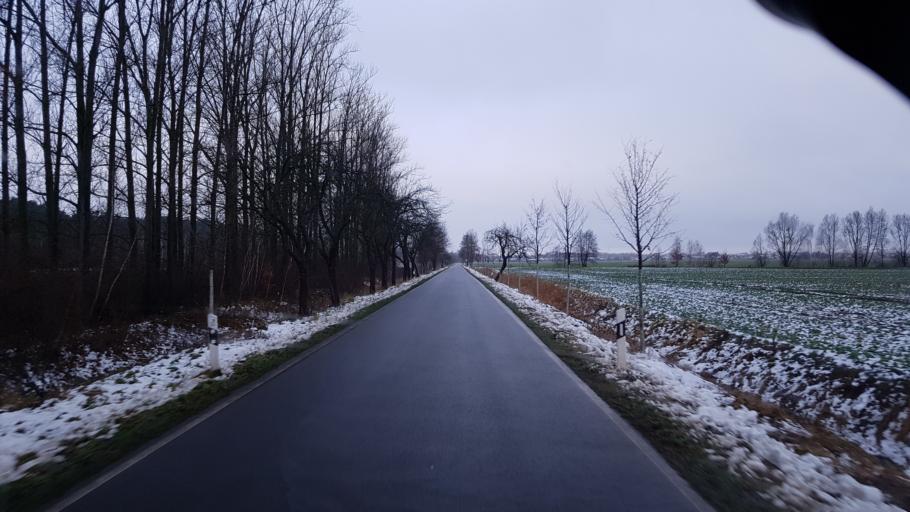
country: DE
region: Brandenburg
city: Luckau
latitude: 51.8099
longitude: 13.7131
